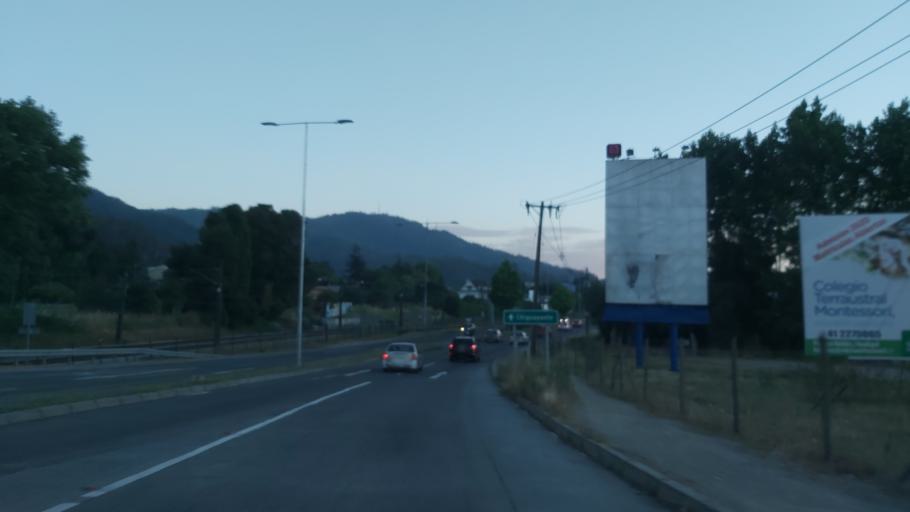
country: CL
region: Biobio
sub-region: Provincia de Concepcion
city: Chiguayante
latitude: -36.8958
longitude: -73.0337
